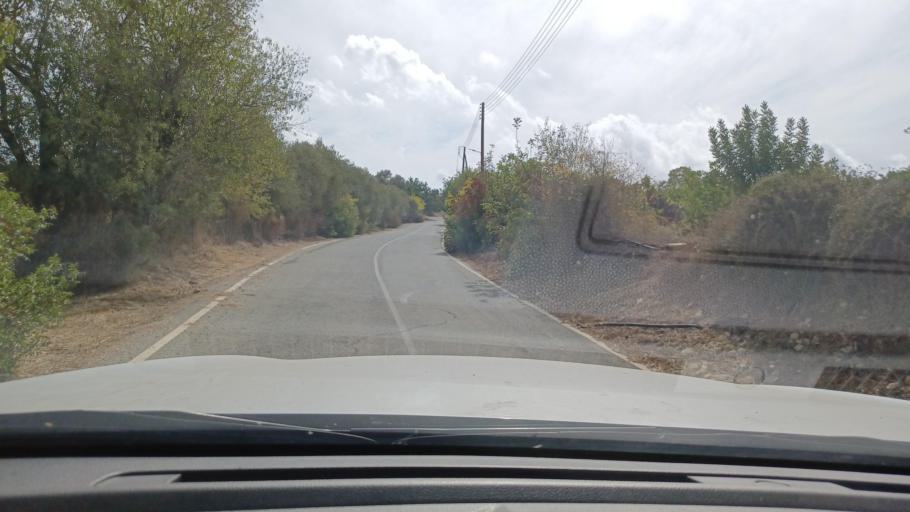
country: CY
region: Pafos
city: Pegeia
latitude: 34.9463
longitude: 32.4457
